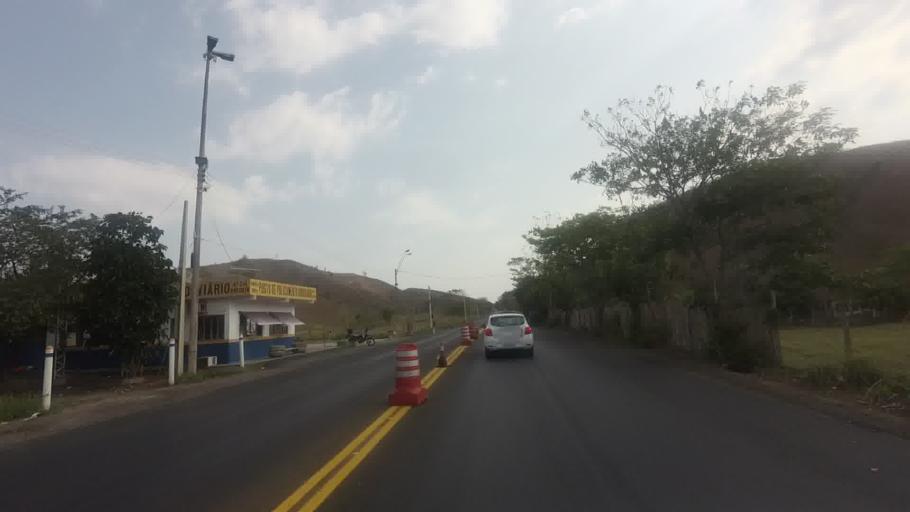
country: BR
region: Rio de Janeiro
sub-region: Bom Jesus Do Itabapoana
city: Bom Jesus do Itabapoana
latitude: -21.2320
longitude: -41.7476
